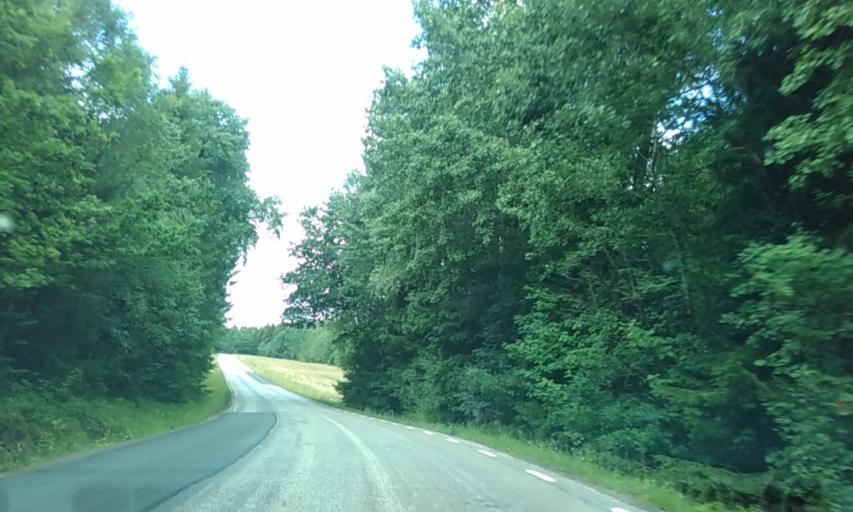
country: SE
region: Vaestra Goetaland
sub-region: Vargarda Kommun
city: Vargarda
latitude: 58.1023
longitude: 12.8213
